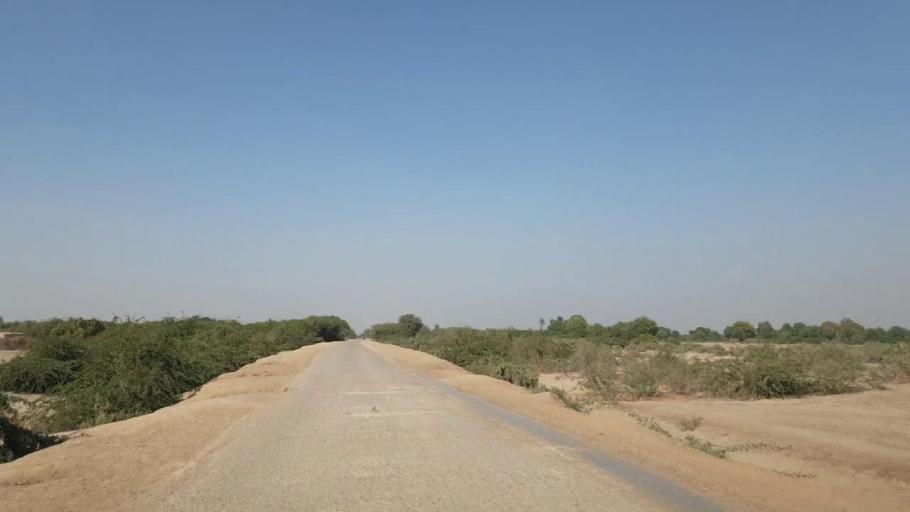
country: PK
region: Sindh
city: Digri
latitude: 24.9903
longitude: 69.1088
